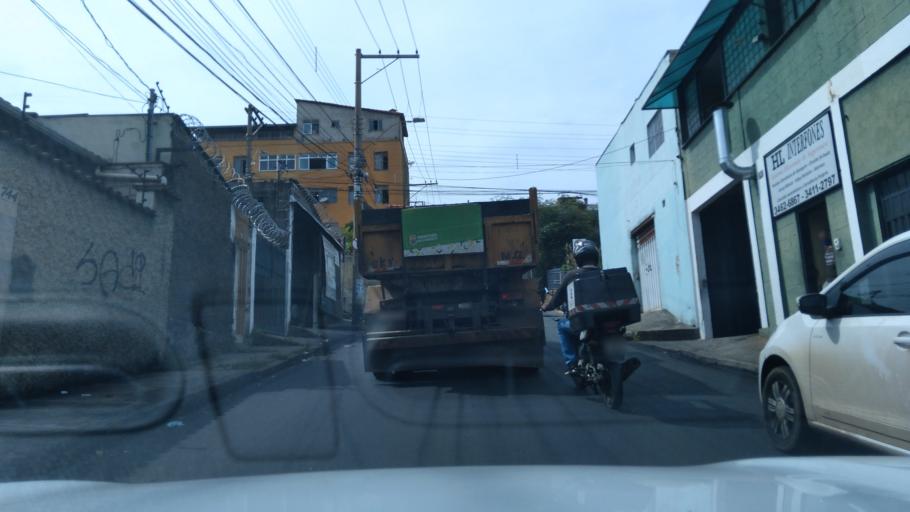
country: BR
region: Minas Gerais
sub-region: Belo Horizonte
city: Belo Horizonte
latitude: -19.9098
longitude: -43.9646
